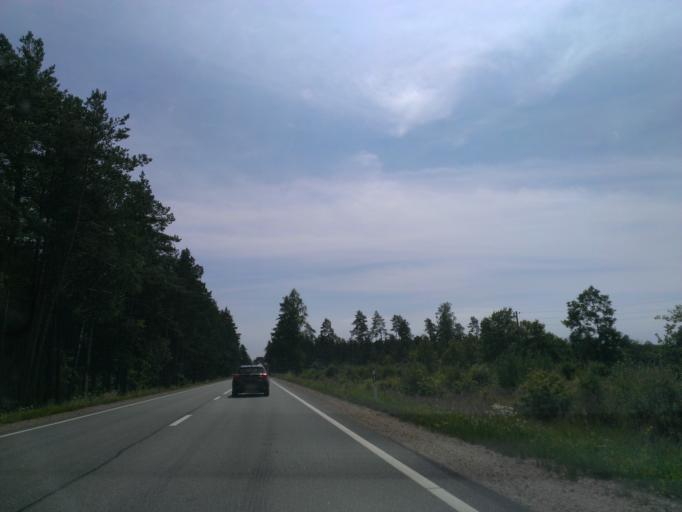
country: LV
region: Salaspils
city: Salaspils
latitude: 56.9347
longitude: 24.3866
